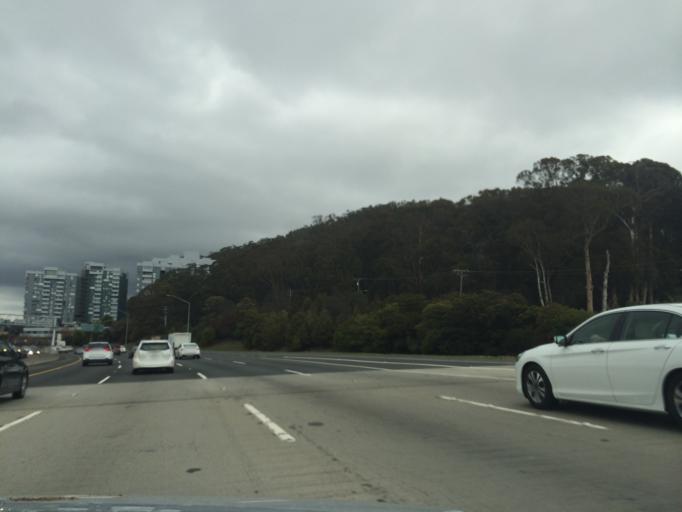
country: US
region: California
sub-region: Alameda County
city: Albany
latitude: 37.8914
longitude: -122.3075
